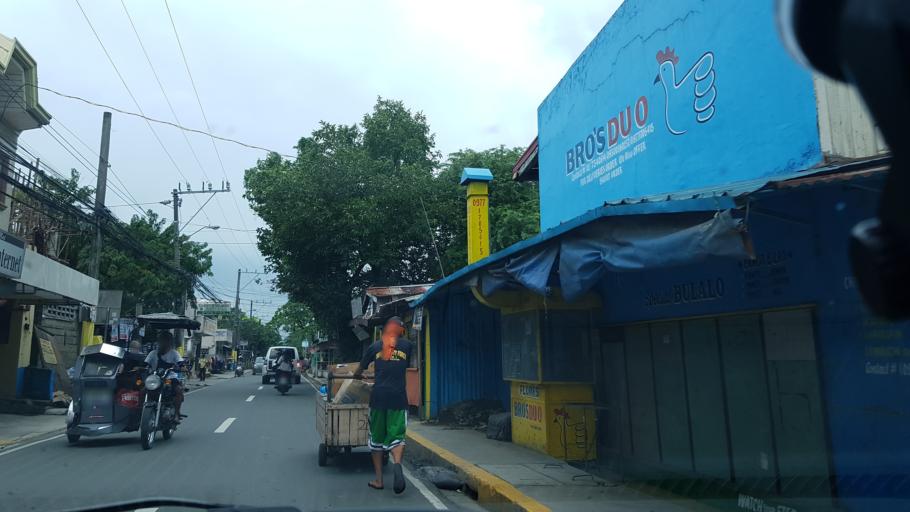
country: PH
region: Calabarzon
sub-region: Province of Rizal
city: Pateros
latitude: 14.5386
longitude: 121.0683
